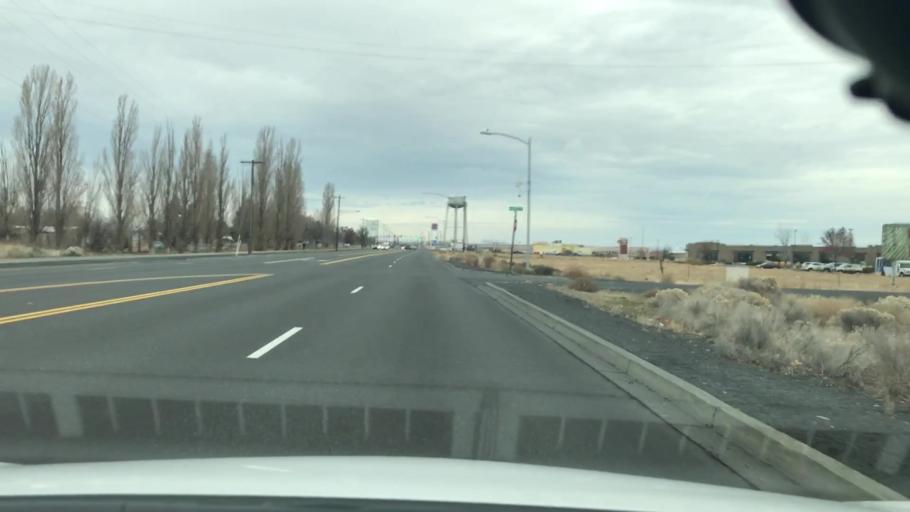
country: US
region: Washington
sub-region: Grant County
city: Cascade Valley
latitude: 47.1600
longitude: -119.3124
